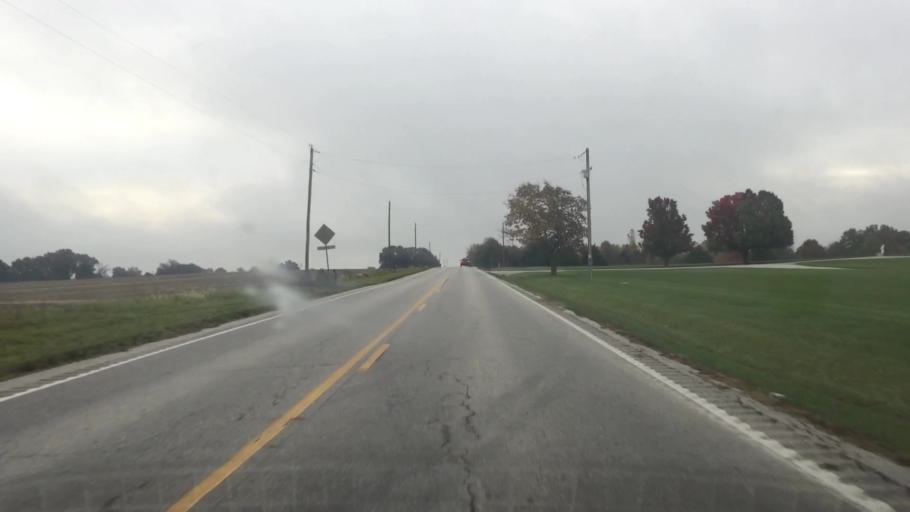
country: US
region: Missouri
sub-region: Boone County
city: Columbia
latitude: 38.9208
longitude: -92.1997
